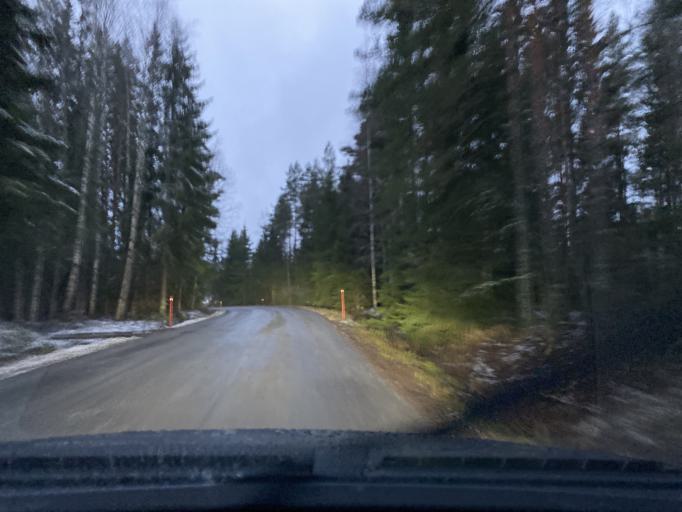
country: FI
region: Pirkanmaa
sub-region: Lounais-Pirkanmaa
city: Punkalaidun
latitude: 61.1543
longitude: 22.9657
